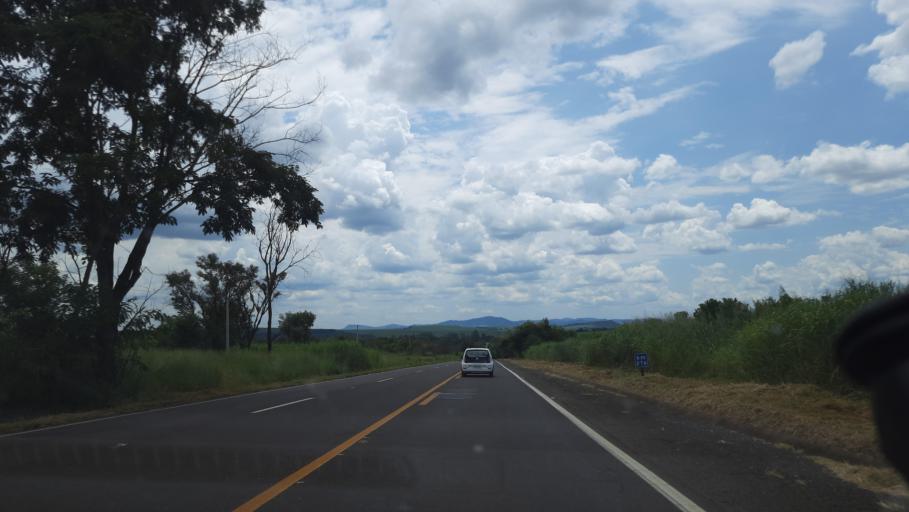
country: BR
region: Sao Paulo
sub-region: Mococa
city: Mococa
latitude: -21.4802
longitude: -47.0857
